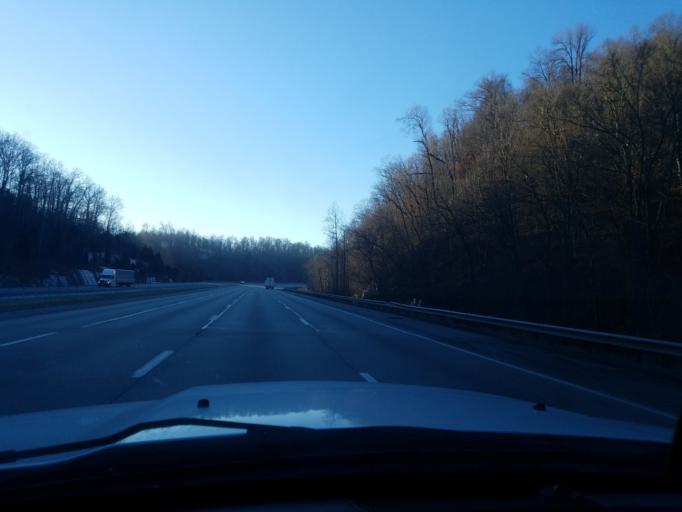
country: US
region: Kentucky
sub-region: Hardin County
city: Elizabethtown
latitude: 37.7494
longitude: -85.7950
